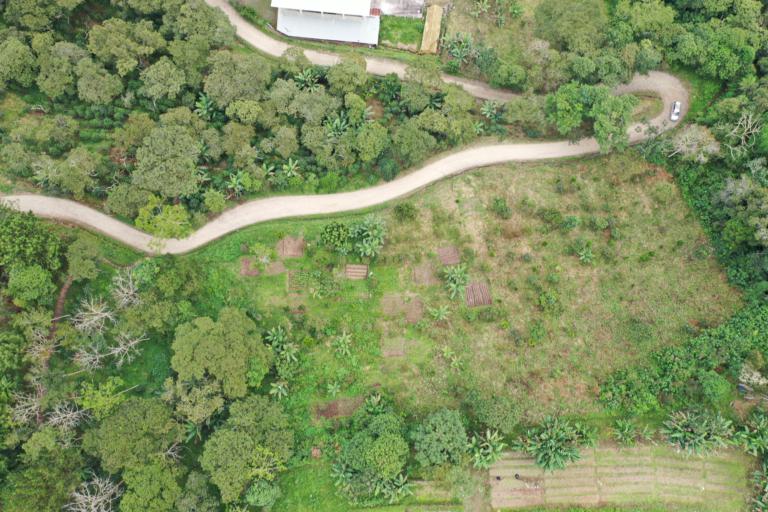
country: BO
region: La Paz
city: Coroico
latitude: -16.2594
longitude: -67.6930
